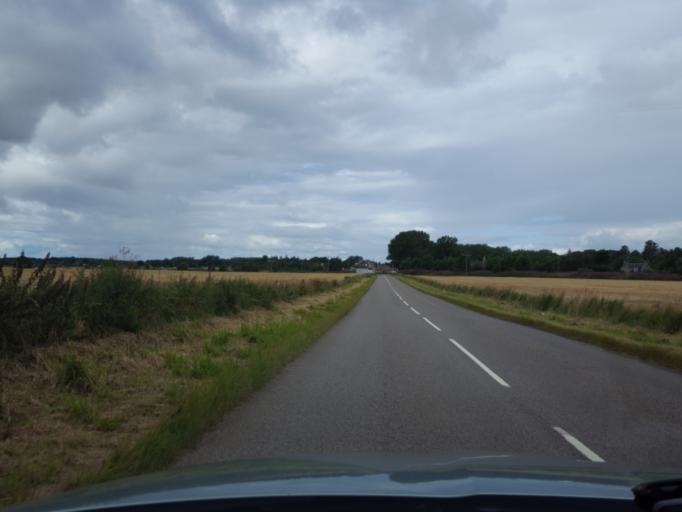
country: GB
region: Scotland
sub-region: Moray
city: Kinloss
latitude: 57.6302
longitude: -3.5536
